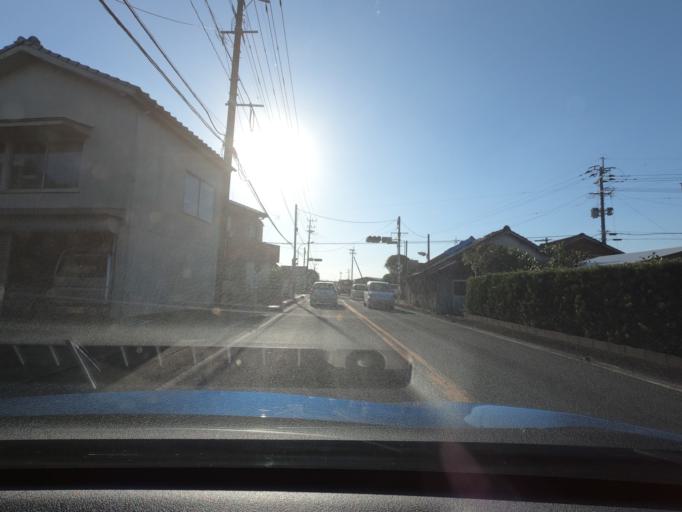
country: JP
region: Kagoshima
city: Izumi
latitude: 32.0848
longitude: 130.2792
